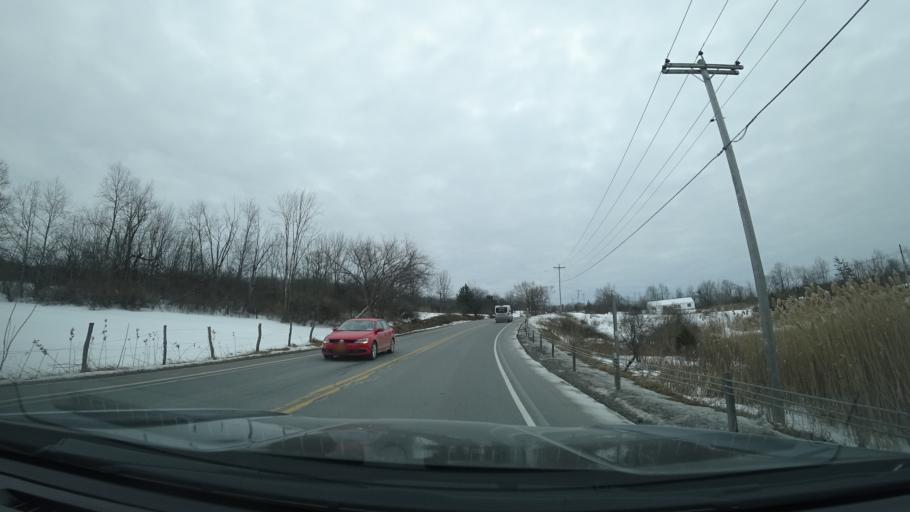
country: US
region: New York
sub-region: Washington County
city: Fort Edward
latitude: 43.2543
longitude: -73.5034
